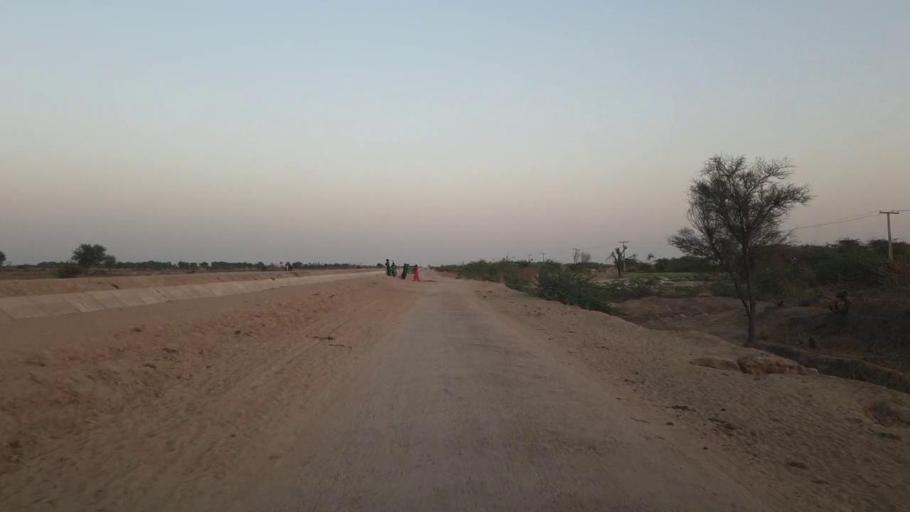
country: PK
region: Sindh
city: Dhoro Naro
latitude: 25.4446
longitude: 69.6310
